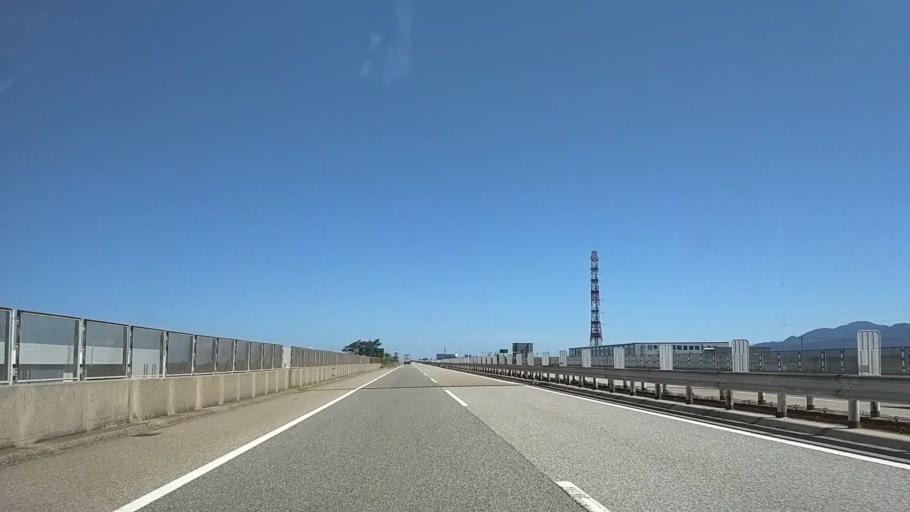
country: JP
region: Toyama
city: Nyuzen
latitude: 36.8864
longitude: 137.4895
